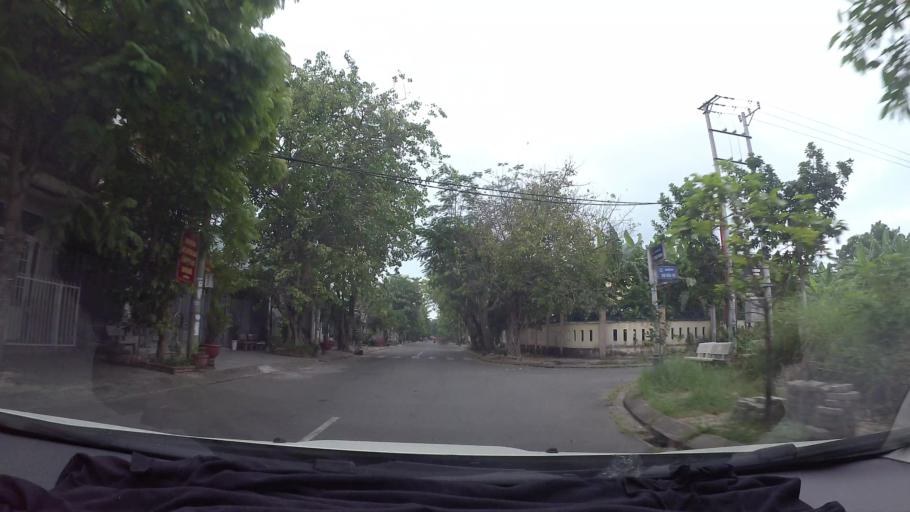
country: VN
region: Da Nang
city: Da Nang
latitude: 16.0847
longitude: 108.2363
